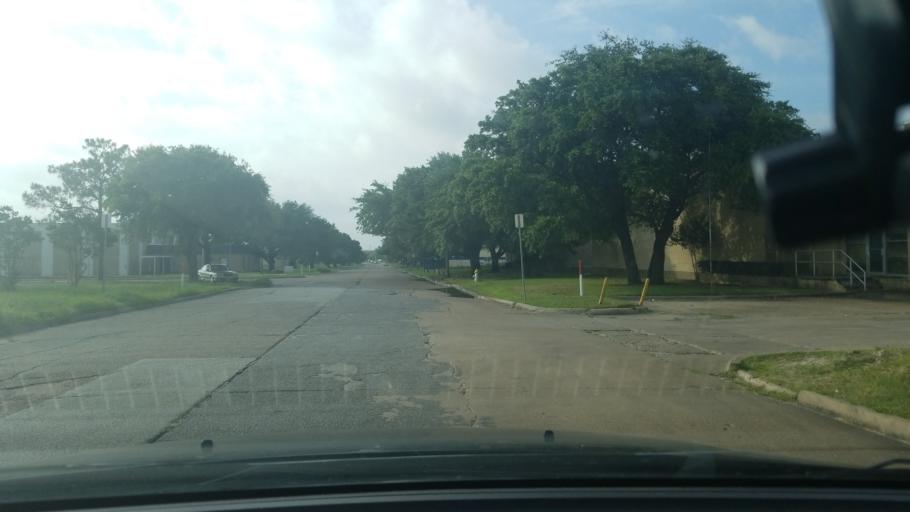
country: US
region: Texas
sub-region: Dallas County
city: Mesquite
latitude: 32.7740
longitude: -96.6531
